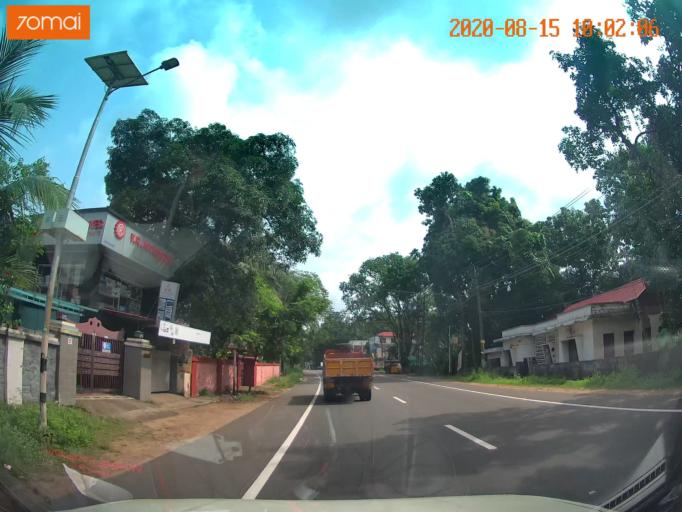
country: IN
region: Kerala
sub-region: Kottayam
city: Changanacheri
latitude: 9.4334
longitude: 76.5438
